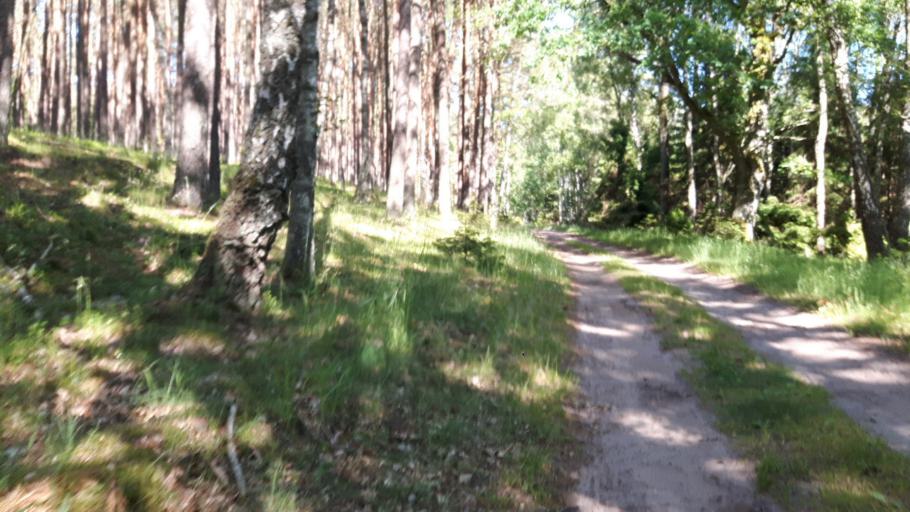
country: PL
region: Pomeranian Voivodeship
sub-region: Powiat leborski
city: Leba
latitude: 54.6990
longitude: 17.4975
